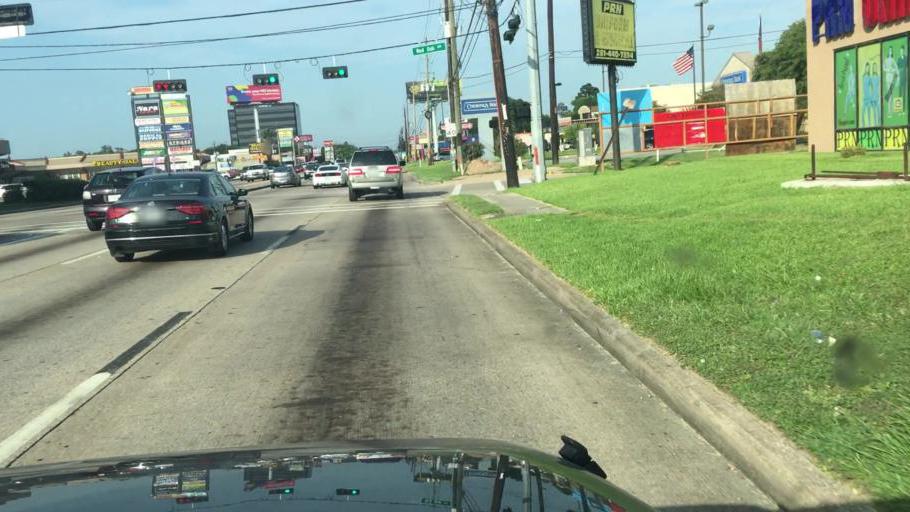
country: US
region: Texas
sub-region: Harris County
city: Spring
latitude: 30.0167
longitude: -95.4439
